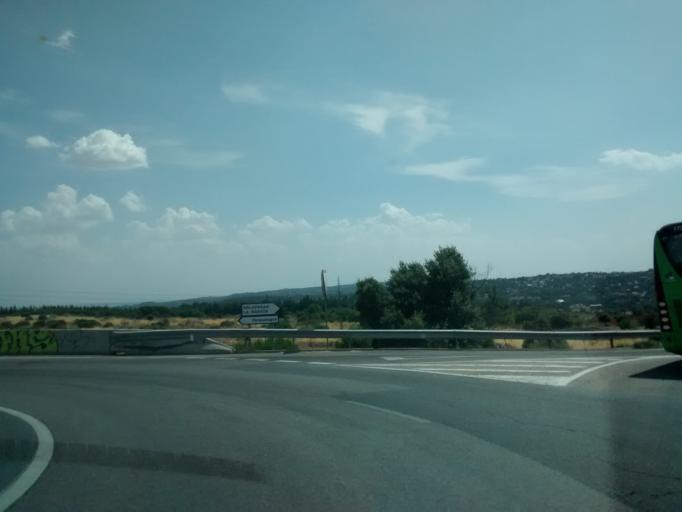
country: ES
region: Madrid
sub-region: Provincia de Madrid
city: Collado-Villalba
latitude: 40.6124
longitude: -3.9800
